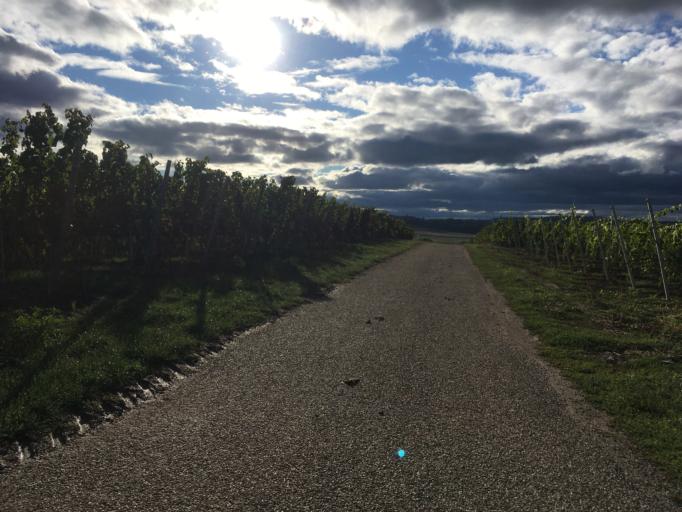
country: DE
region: Baden-Wuerttemberg
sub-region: Regierungsbezirk Stuttgart
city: Brackenheim
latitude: 49.0878
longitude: 9.0676
